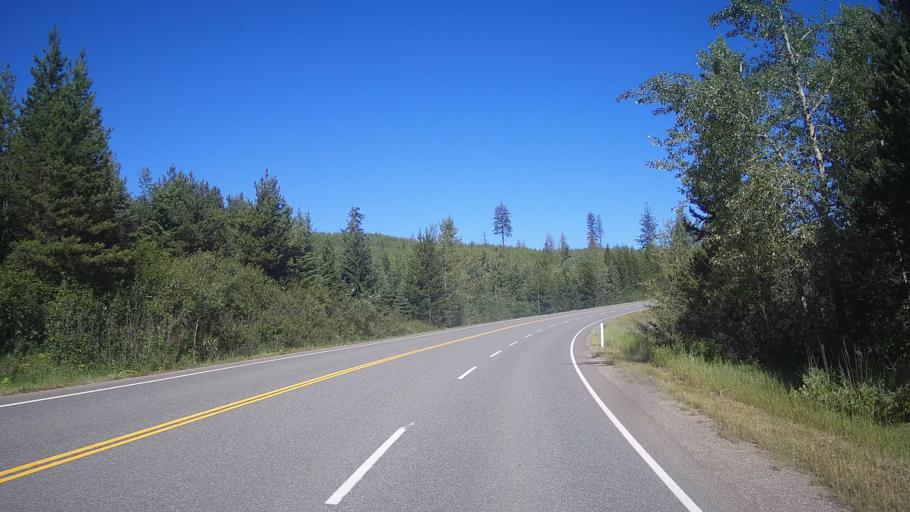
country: CA
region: British Columbia
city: Kamloops
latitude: 51.4872
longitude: -120.3206
